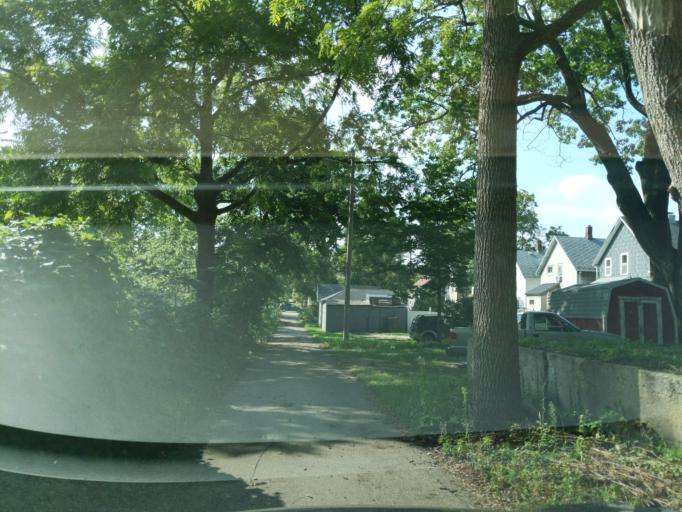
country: US
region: Michigan
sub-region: Ingham County
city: Lansing
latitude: 42.7286
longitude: -84.5364
